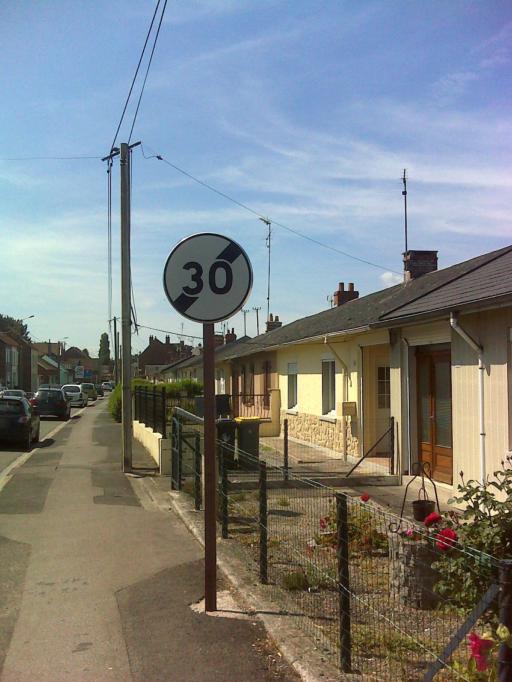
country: FR
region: Nord-Pas-de-Calais
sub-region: Departement du Nord
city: Aulnoye-Aymeries
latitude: 50.2043
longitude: 3.8510
